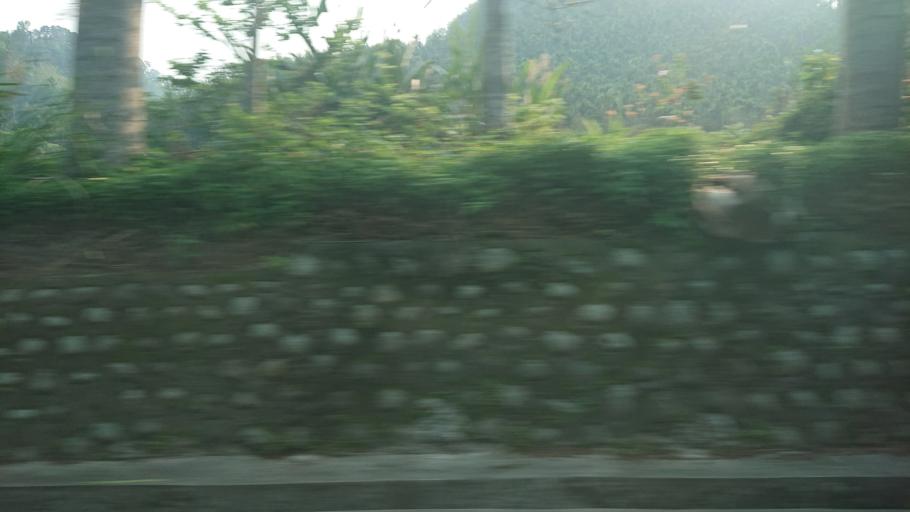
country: TW
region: Taiwan
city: Daxi
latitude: 24.8669
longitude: 121.4153
